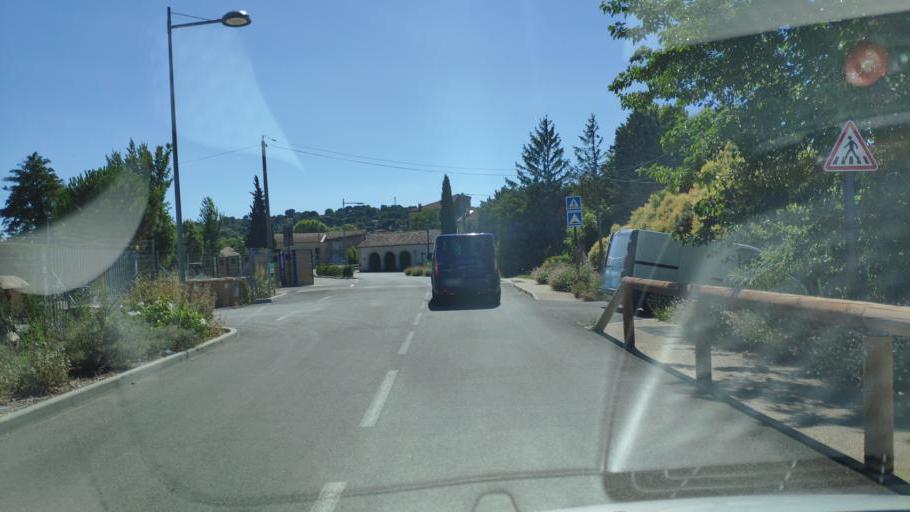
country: FR
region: Provence-Alpes-Cote d'Azur
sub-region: Departement du Vaucluse
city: Chateauneuf-de-Gadagne
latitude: 43.9282
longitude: 4.9517
